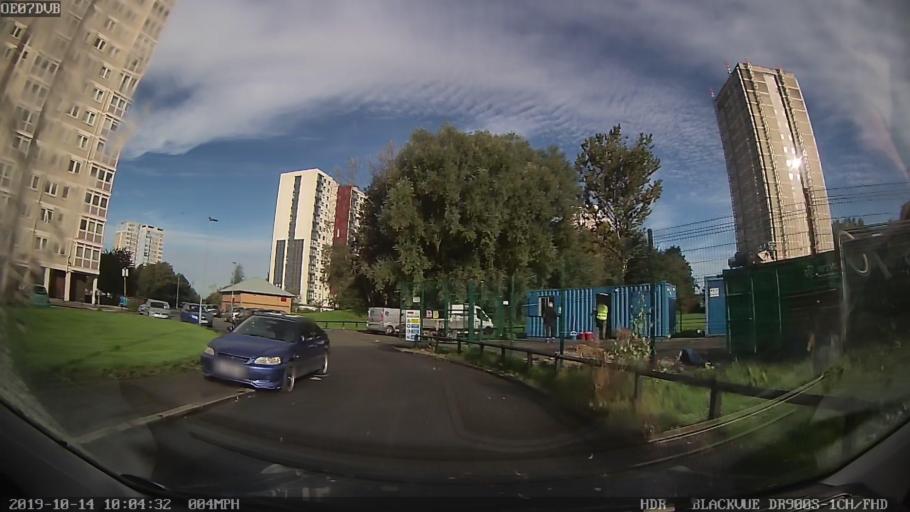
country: GB
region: England
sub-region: Borough of Rochdale
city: Middleton
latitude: 53.5275
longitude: -2.1905
